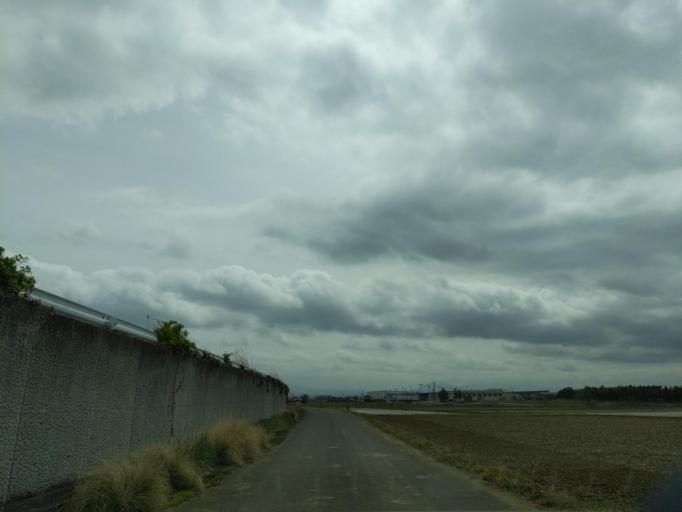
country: JP
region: Fukushima
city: Koriyama
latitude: 37.3747
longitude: 140.3160
